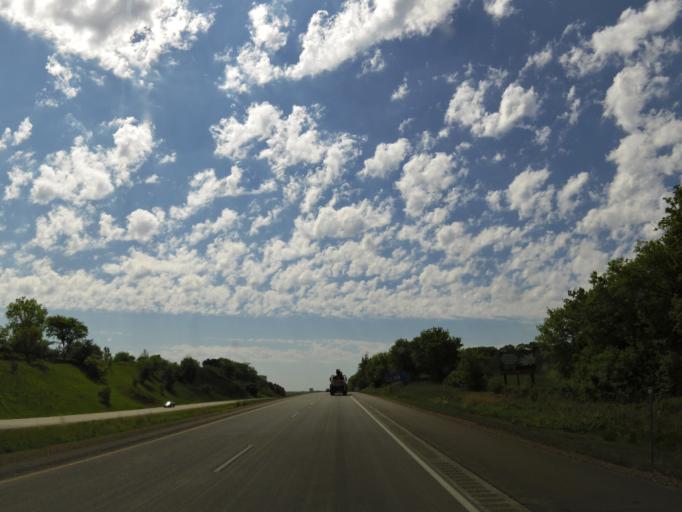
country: US
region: Wisconsin
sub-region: Eau Claire County
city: Eau Claire
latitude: 44.8041
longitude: -91.5571
